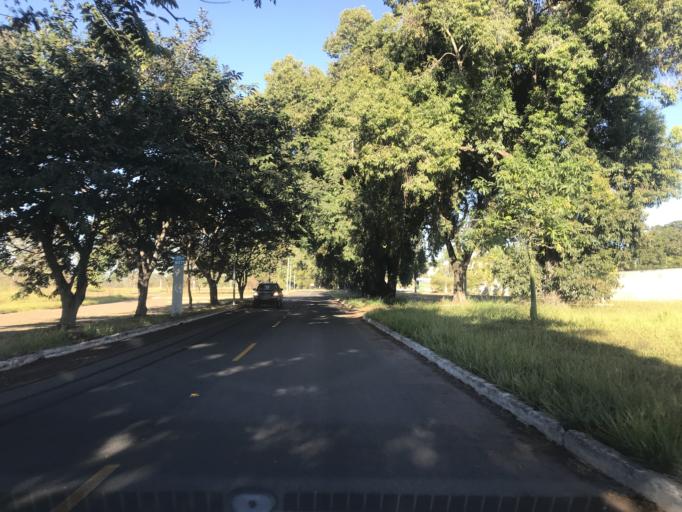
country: BR
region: Federal District
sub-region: Brasilia
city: Brasilia
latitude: -15.8238
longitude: -47.8911
